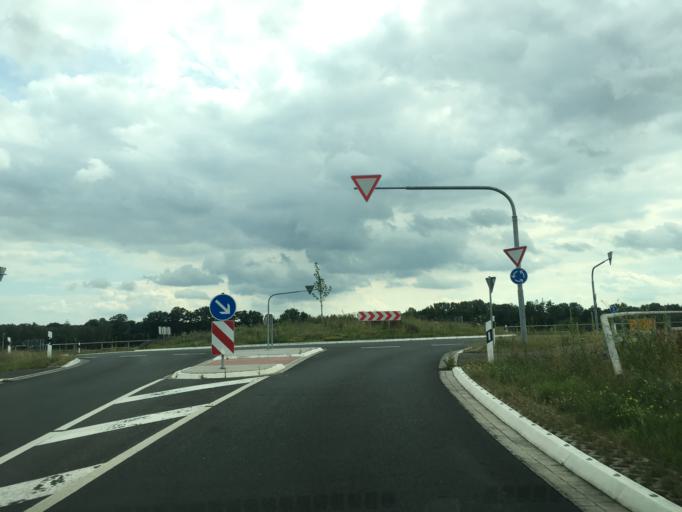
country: DE
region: North Rhine-Westphalia
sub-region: Regierungsbezirk Munster
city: Telgte
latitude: 51.8989
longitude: 7.7357
